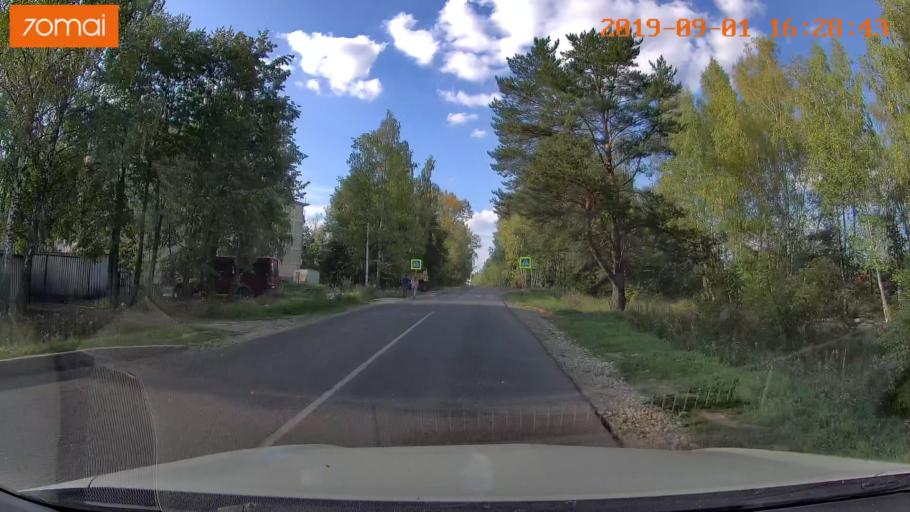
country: RU
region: Kaluga
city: Maloyaroslavets
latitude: 54.9290
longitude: 36.4718
